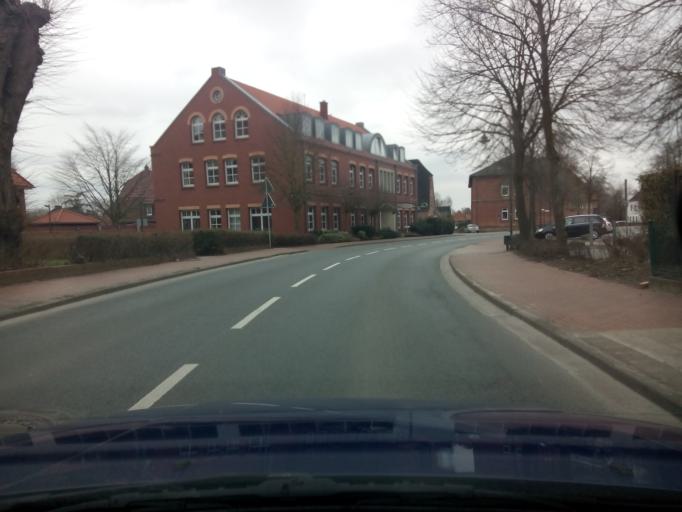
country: DE
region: Lower Saxony
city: Osterholz-Scharmbeck
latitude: 53.2256
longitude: 8.8129
